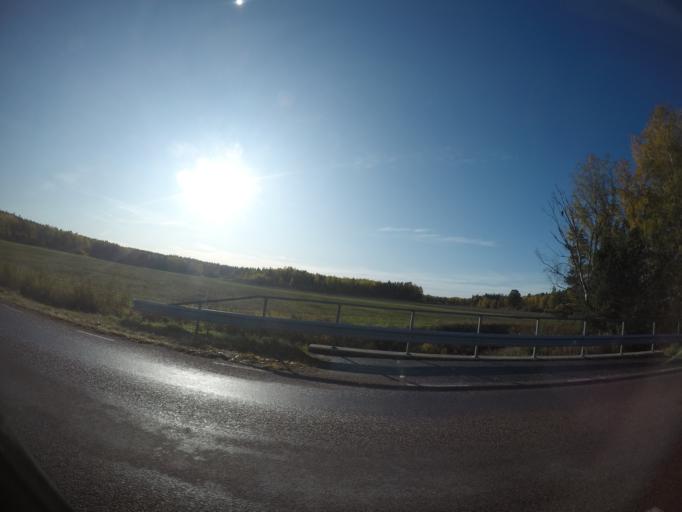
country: SE
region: Soedermanland
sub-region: Eskilstuna Kommun
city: Kvicksund
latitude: 59.4098
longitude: 16.2641
